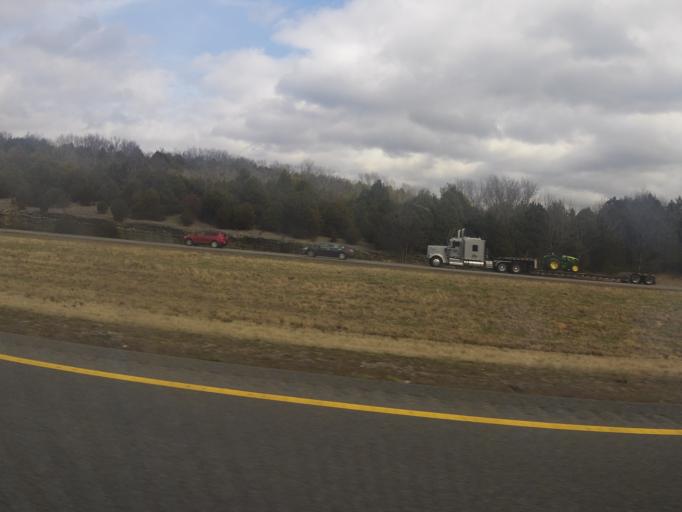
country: US
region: Tennessee
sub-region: Rutherford County
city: Plainview
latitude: 35.6921
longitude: -86.2976
